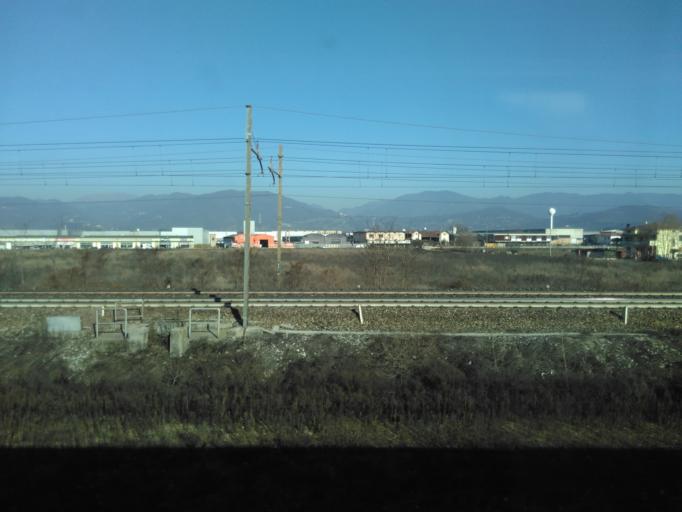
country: IT
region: Lombardy
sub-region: Provincia di Brescia
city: Roncadelle
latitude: 45.5468
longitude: 10.1447
